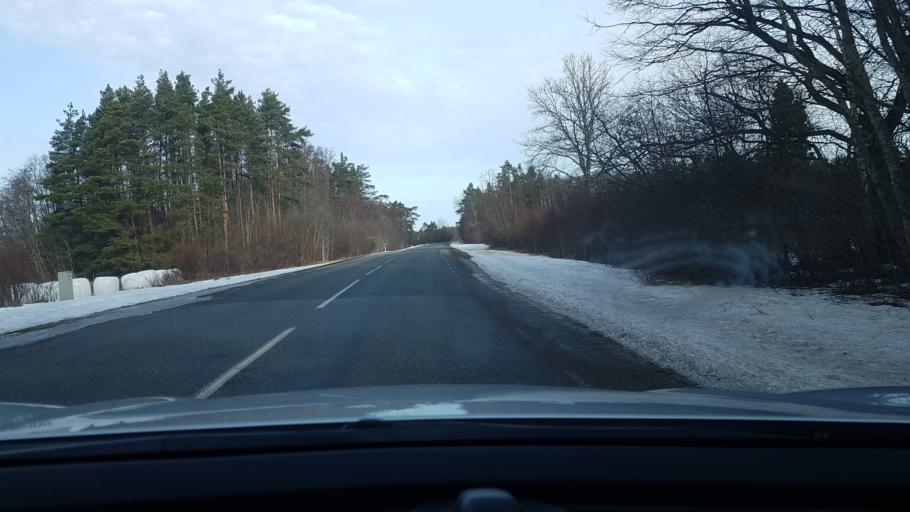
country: EE
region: Saare
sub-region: Kuressaare linn
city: Kuressaare
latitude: 58.4000
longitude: 22.6426
